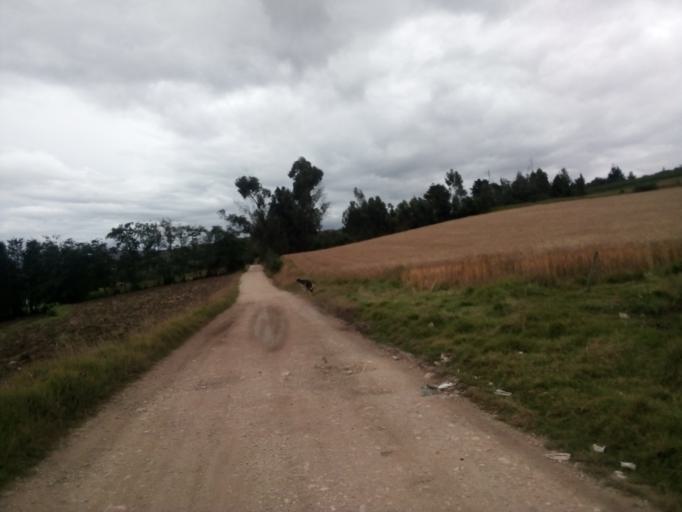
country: CO
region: Boyaca
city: Toca
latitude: 5.5740
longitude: -73.1559
